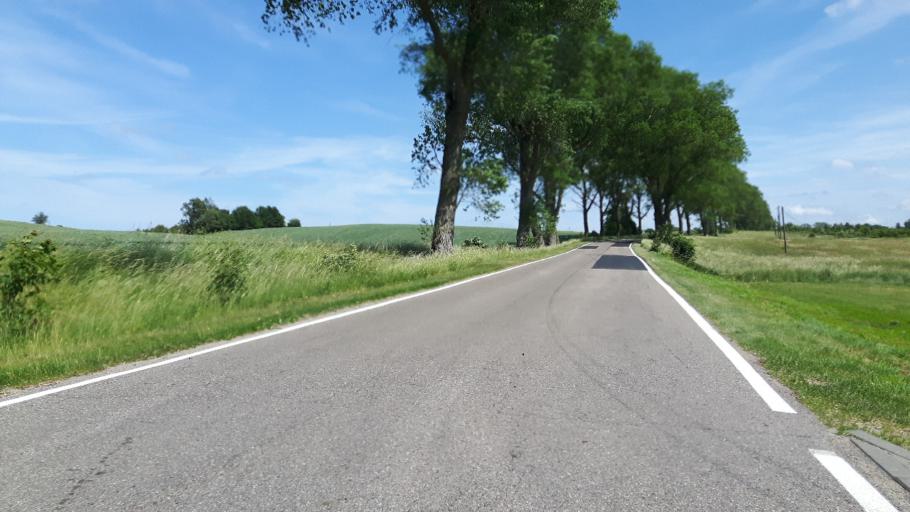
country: PL
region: Pomeranian Voivodeship
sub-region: Powiat wejherowski
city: Gniewino
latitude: 54.7201
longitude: 17.9935
